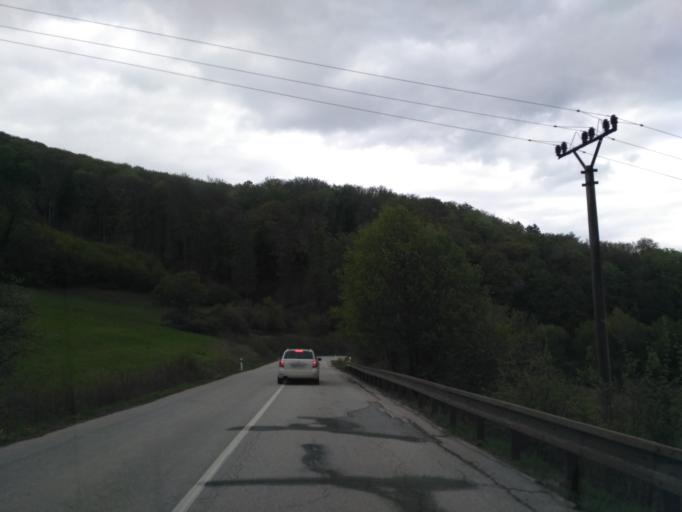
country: SK
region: Kosicky
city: Dobsina
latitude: 48.6414
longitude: 20.3577
